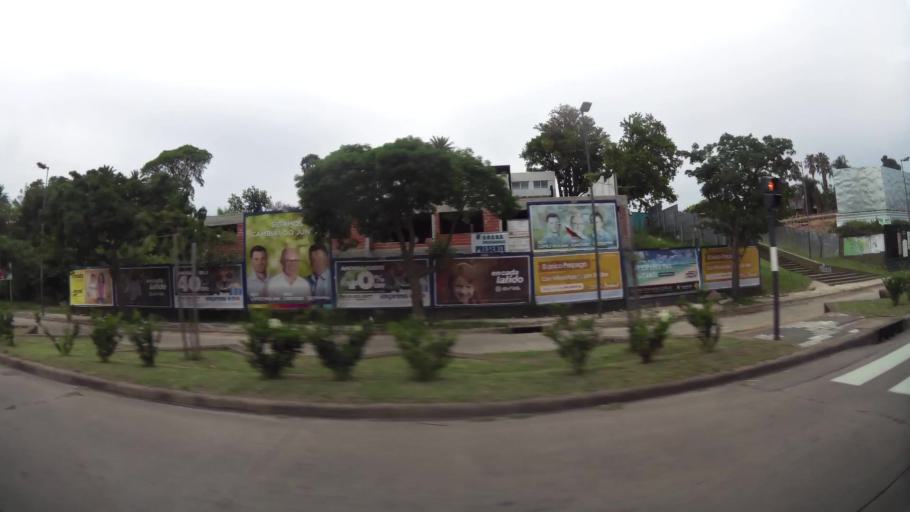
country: AR
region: Santa Fe
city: Granadero Baigorria
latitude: -32.9011
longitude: -60.6824
